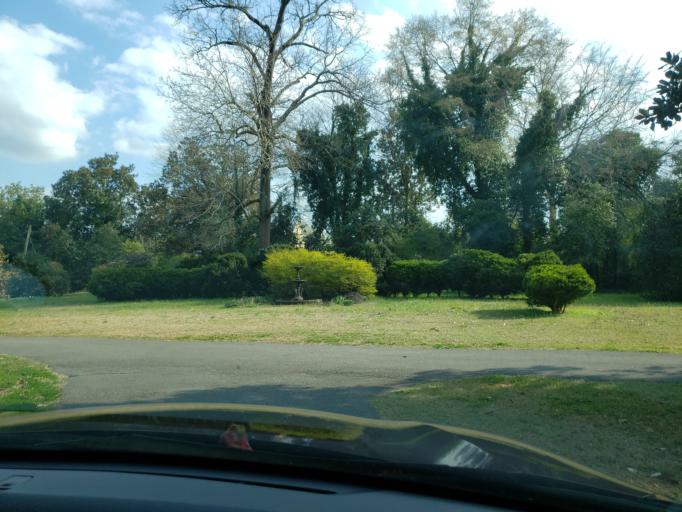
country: US
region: Alabama
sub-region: Hale County
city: Greensboro
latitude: 32.7040
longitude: -87.6079
